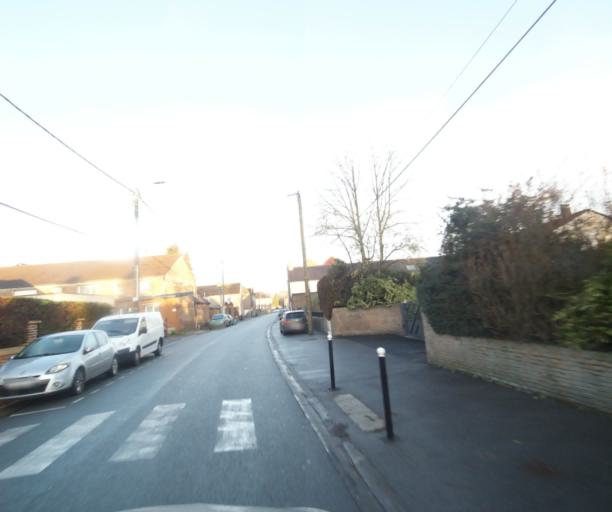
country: FR
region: Nord-Pas-de-Calais
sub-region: Departement du Nord
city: Onnaing
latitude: 50.3838
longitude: 3.6034
